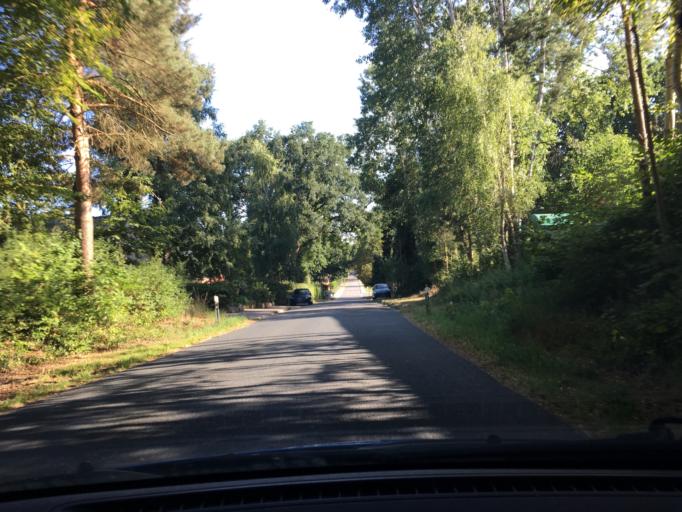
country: DE
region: Lower Saxony
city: Thomasburg
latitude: 53.2276
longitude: 10.7035
